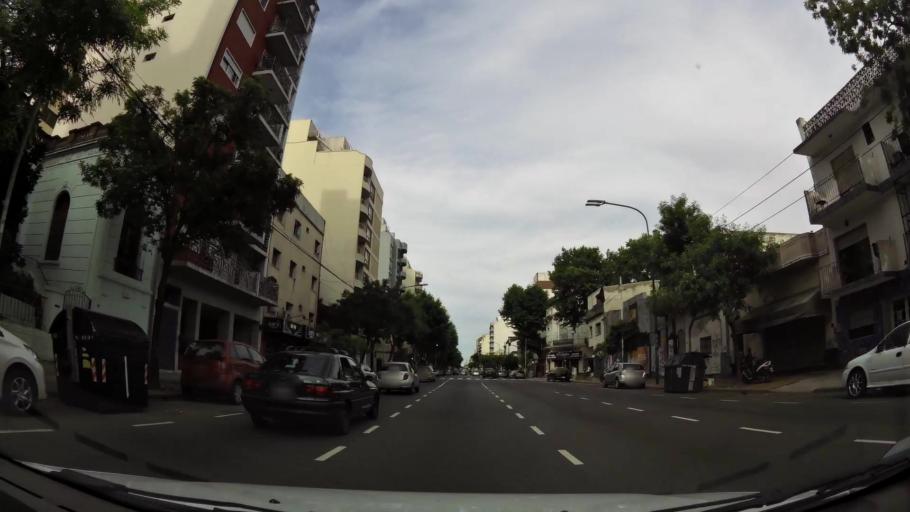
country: AR
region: Buenos Aires F.D.
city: Villa Santa Rita
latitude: -34.6354
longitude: -58.4668
